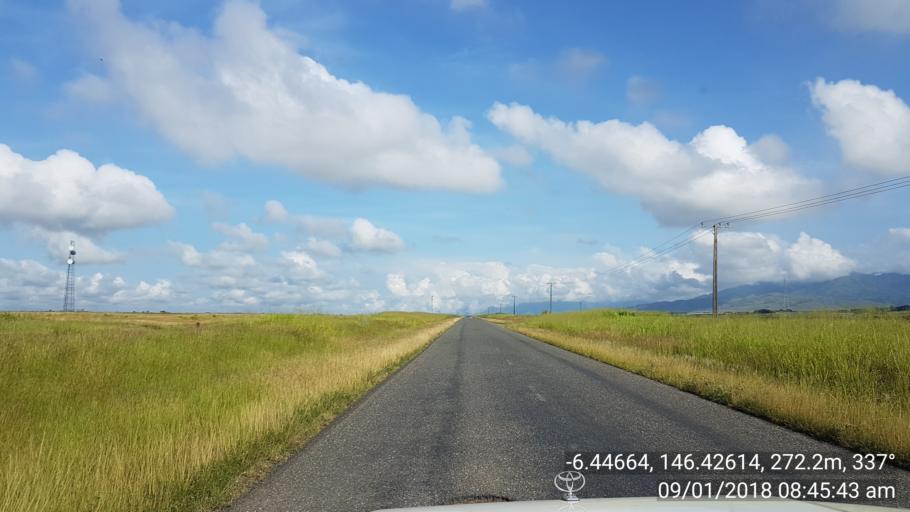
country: PG
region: Eastern Highlands
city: Kainantu
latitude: -6.4467
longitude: 146.4259
